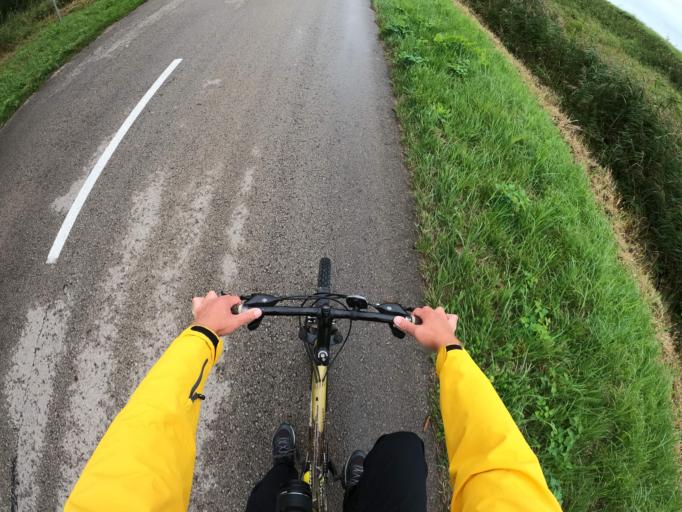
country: LT
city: Rusne
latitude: 55.3342
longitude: 21.3697
